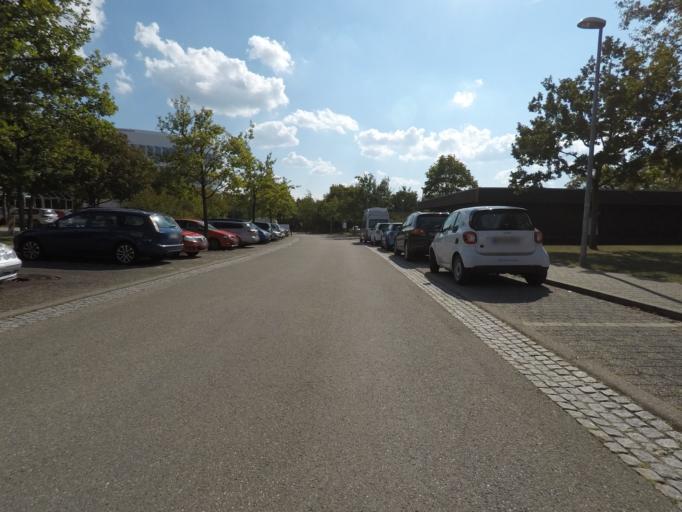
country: DE
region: Baden-Wuerttemberg
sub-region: Regierungsbezirk Stuttgart
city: Gerlingen
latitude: 48.7409
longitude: 9.0955
